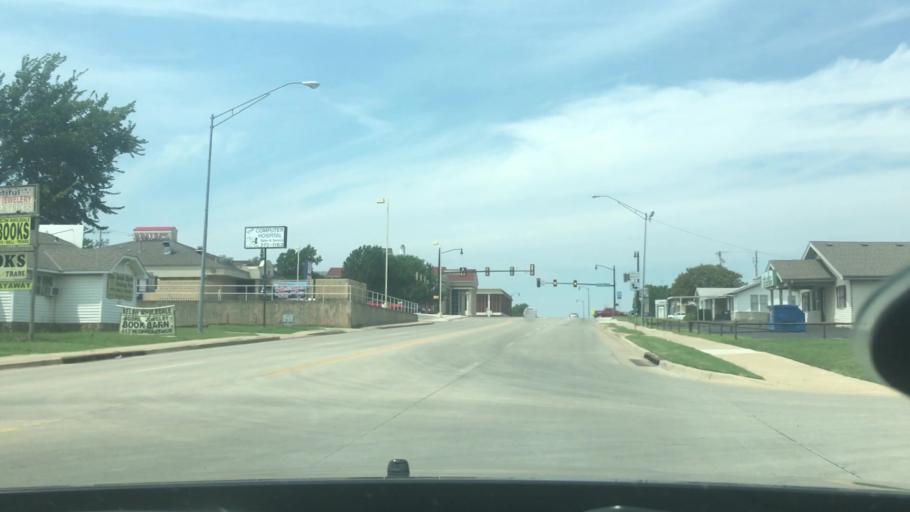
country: US
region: Oklahoma
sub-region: Pottawatomie County
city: Shawnee
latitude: 35.3618
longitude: -96.9281
